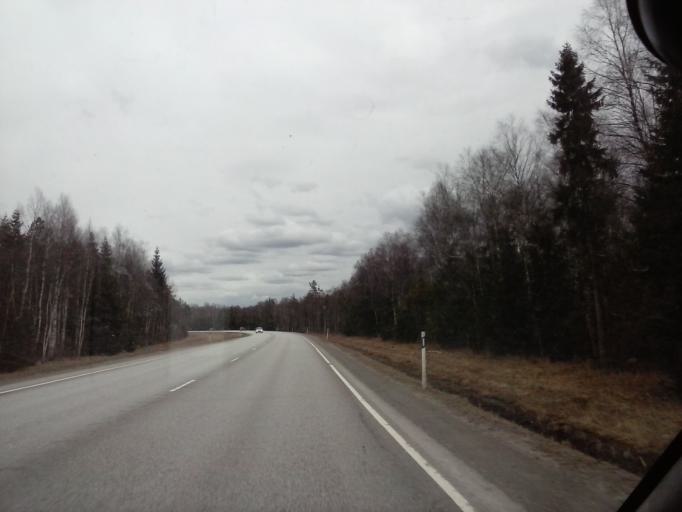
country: EE
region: Jaervamaa
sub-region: Paide linn
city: Paide
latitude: 59.0310
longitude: 25.4846
